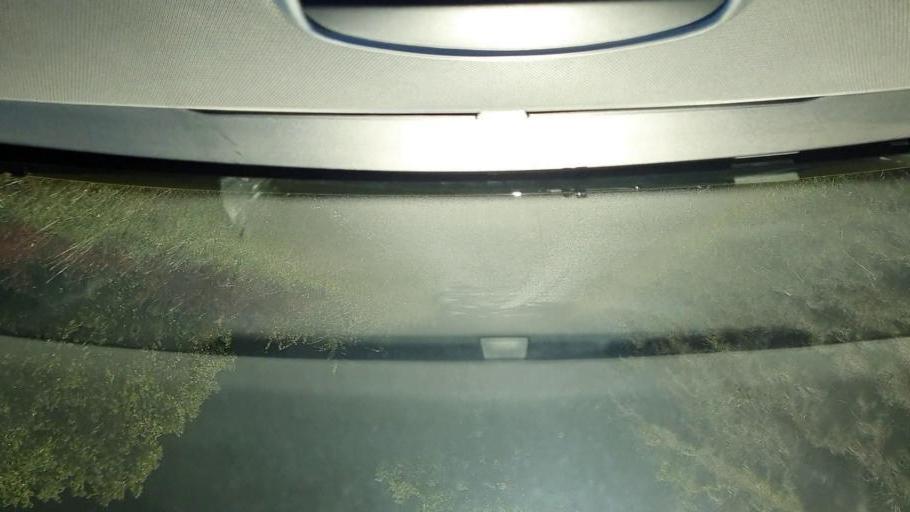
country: FR
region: Languedoc-Roussillon
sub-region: Departement du Gard
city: Sumene
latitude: 43.9838
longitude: 3.7483
